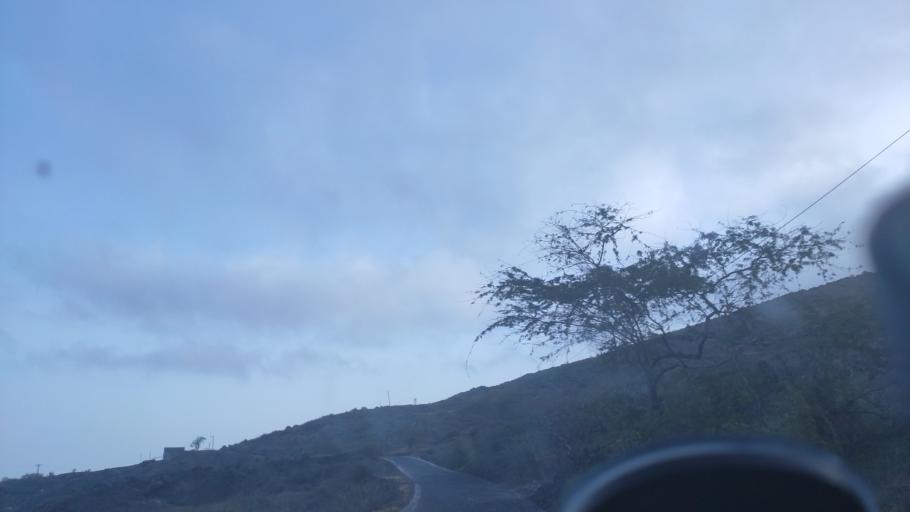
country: CV
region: Mosteiros
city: Porto dos Mosteiros
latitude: 15.0082
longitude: -24.3057
